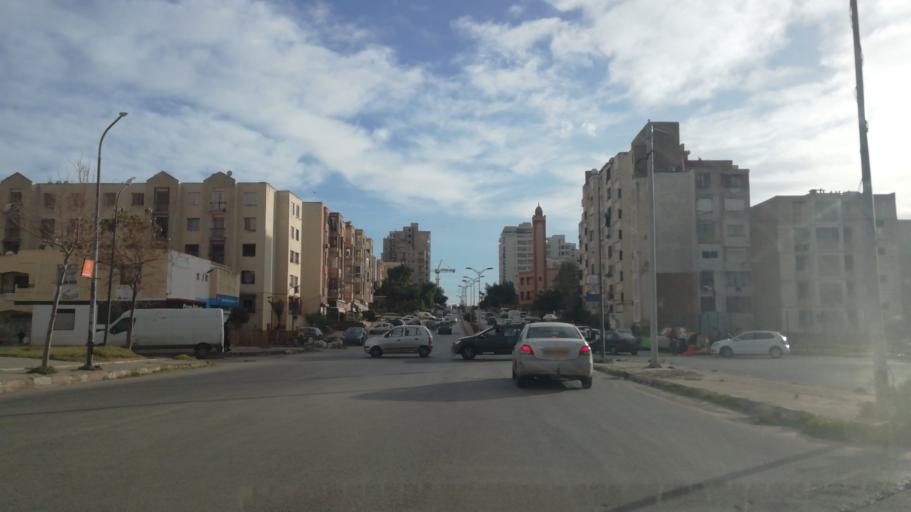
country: DZ
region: Oran
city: Bir el Djir
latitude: 35.7203
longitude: -0.5958
